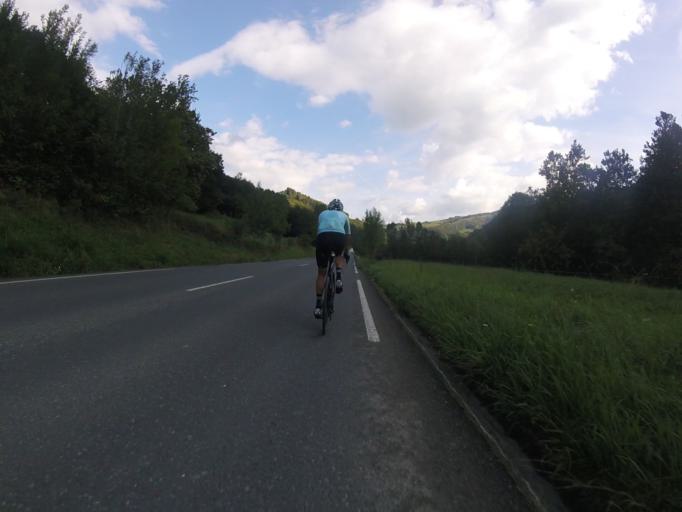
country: ES
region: Basque Country
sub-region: Provincia de Guipuzcoa
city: Amezqueta
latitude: 43.0593
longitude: -2.0877
